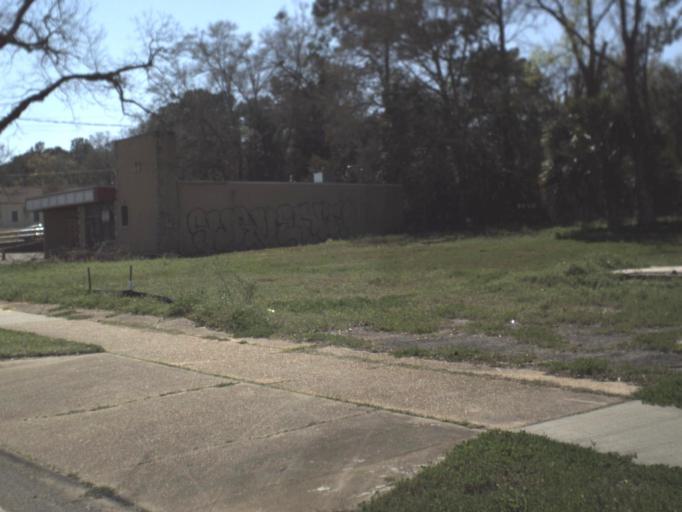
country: US
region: Florida
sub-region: Leon County
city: Tallahassee
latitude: 30.4244
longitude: -84.3024
